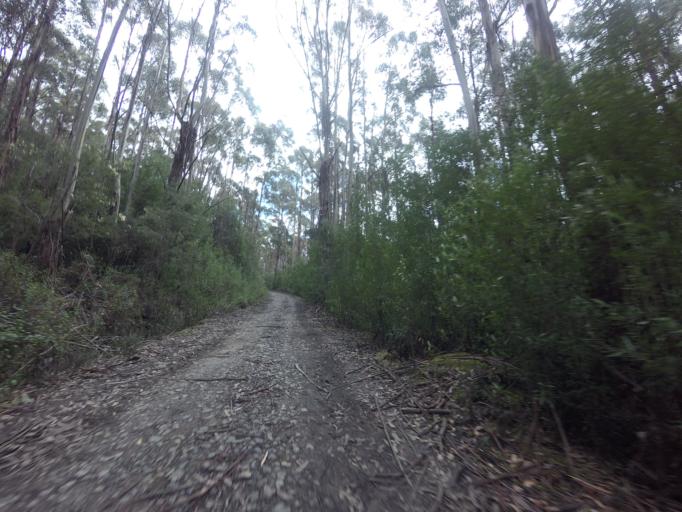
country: AU
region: Tasmania
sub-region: Huon Valley
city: Geeveston
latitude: -43.4042
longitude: 147.0106
